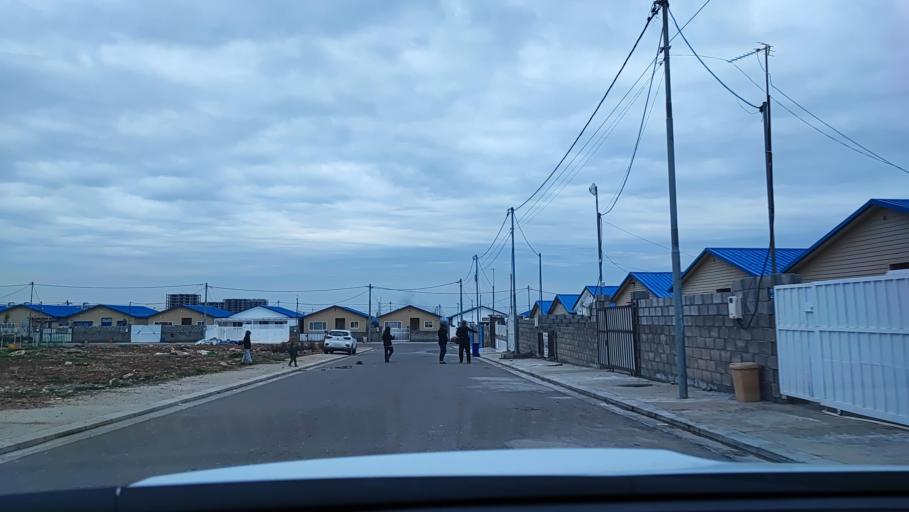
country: IQ
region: Arbil
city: Erbil
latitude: 36.2861
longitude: 44.0814
